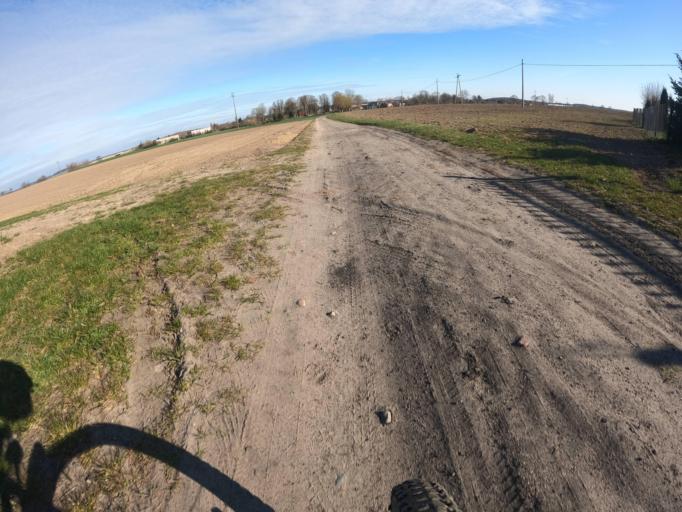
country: PL
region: West Pomeranian Voivodeship
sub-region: Powiat kolobrzeski
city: Ryman
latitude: 54.0029
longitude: 15.4893
